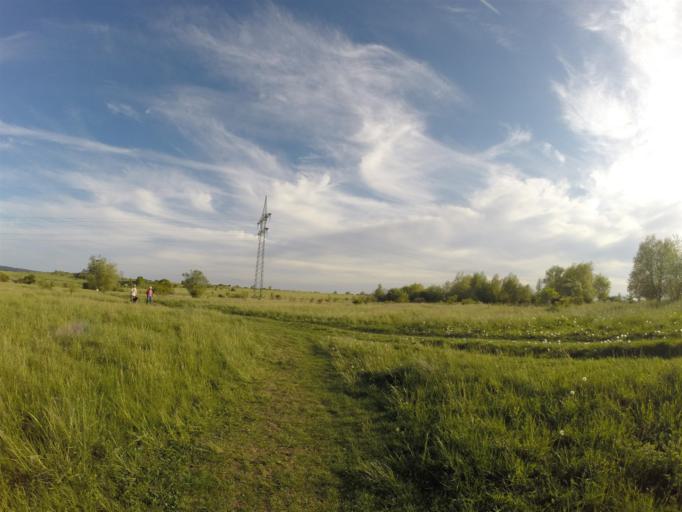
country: DE
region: Thuringia
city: Lehesten
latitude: 50.9565
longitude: 11.5697
